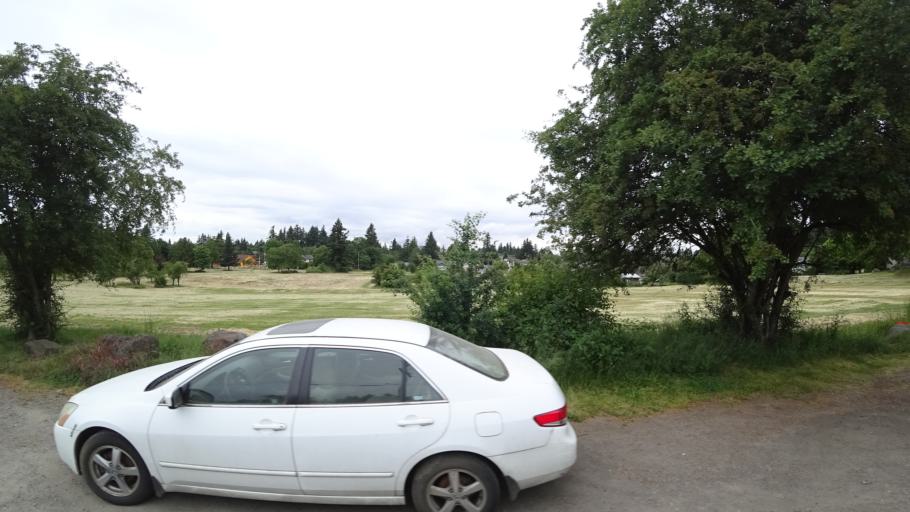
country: US
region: Oregon
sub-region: Clackamas County
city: Happy Valley
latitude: 45.4887
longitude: -122.5214
